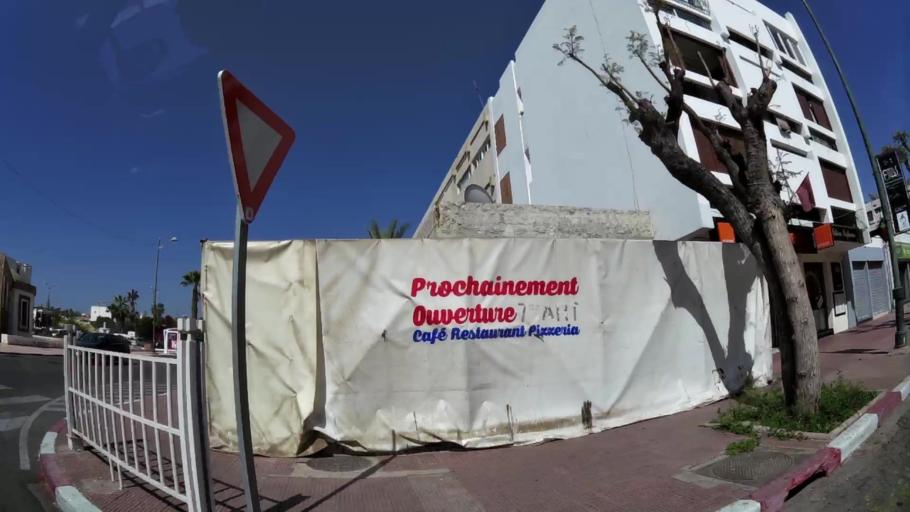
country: MA
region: Souss-Massa-Draa
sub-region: Agadir-Ida-ou-Tnan
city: Agadir
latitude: 30.4233
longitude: -9.6003
